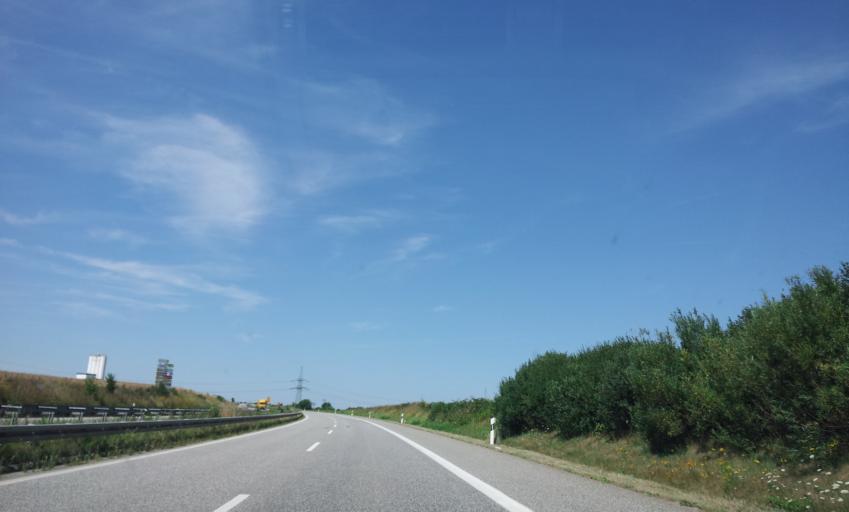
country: DE
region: Mecklenburg-Vorpommern
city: Wendorf
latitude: 54.2762
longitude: 13.0794
